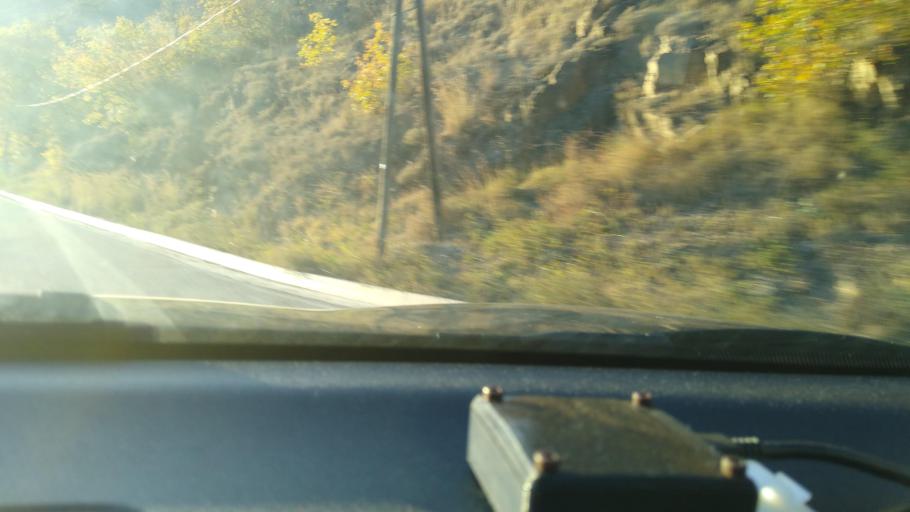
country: FR
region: Languedoc-Roussillon
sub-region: Departement des Pyrenees-Orientales
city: Vernet-les-Bains
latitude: 42.5691
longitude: 2.3277
